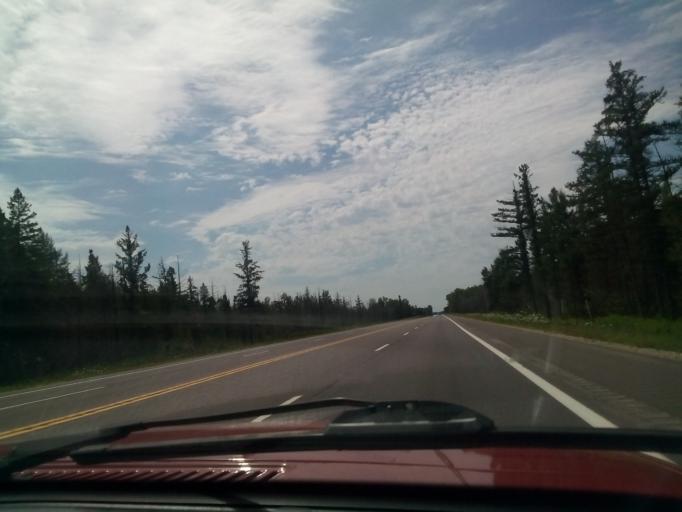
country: US
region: Michigan
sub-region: Schoolcraft County
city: Manistique
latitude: 46.0217
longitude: -85.9871
